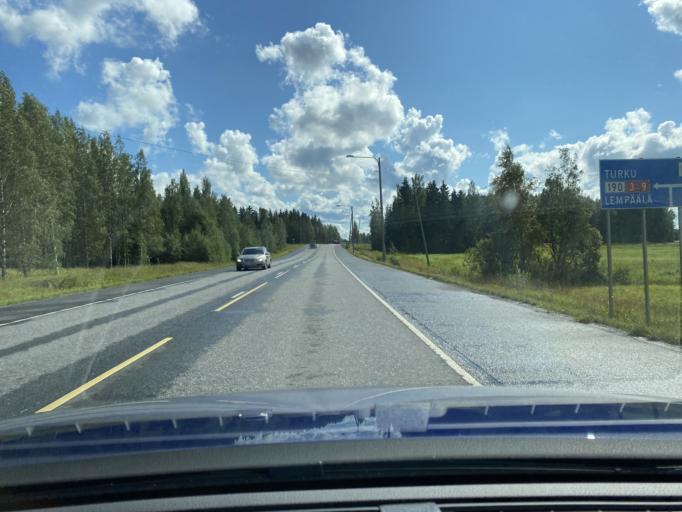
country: FI
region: Pirkanmaa
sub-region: Tampere
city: Lempaeaelae
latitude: 61.3286
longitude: 23.7755
